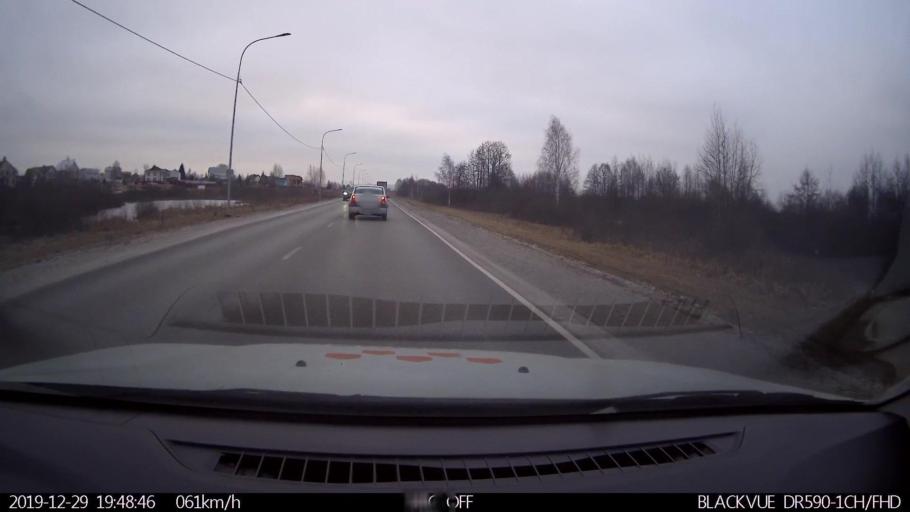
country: RU
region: Nizjnij Novgorod
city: Neklyudovo
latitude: 56.3832
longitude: 44.0099
